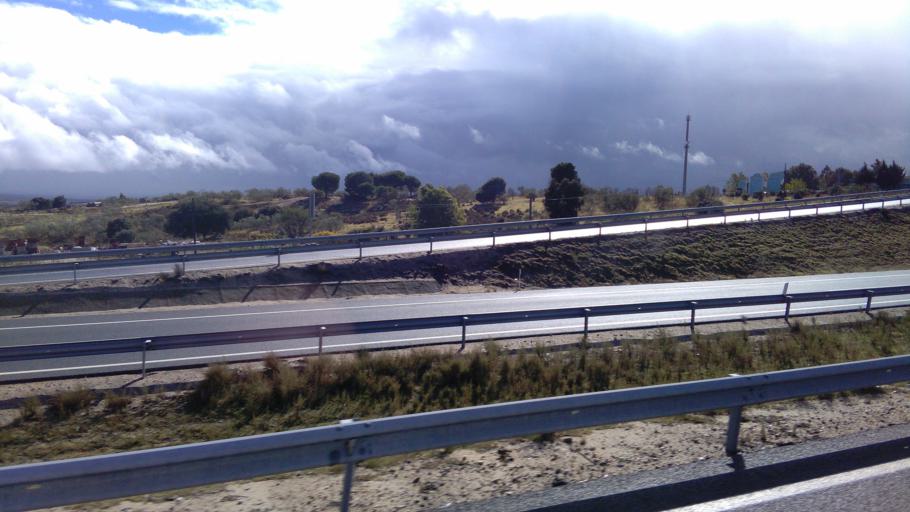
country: ES
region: Castille-La Mancha
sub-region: Province of Toledo
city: Valmojado
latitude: 40.2477
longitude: -4.0565
